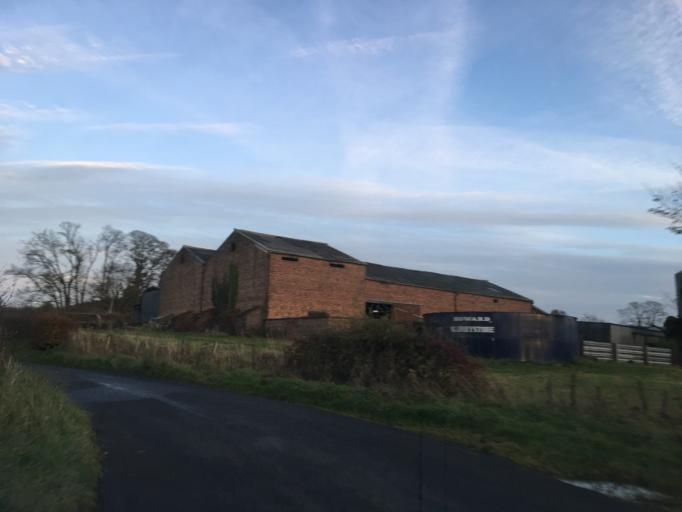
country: GB
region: Scotland
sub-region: Fife
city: Saline
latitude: 56.1239
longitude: -3.5899
